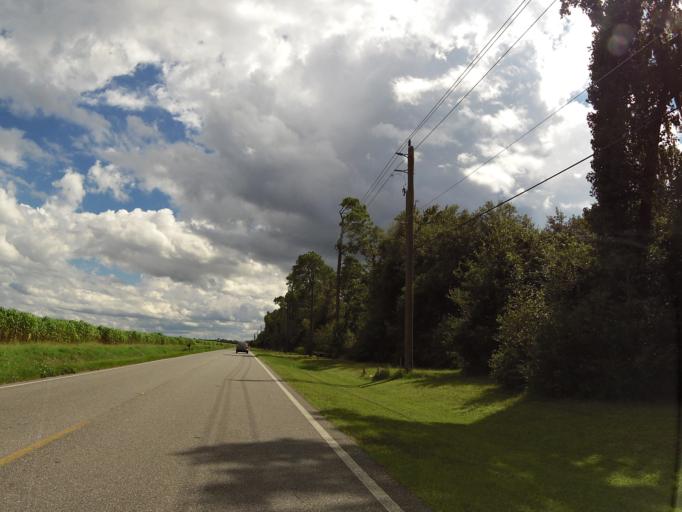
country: US
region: Florida
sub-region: Saint Johns County
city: Saint Augustine South
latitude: 29.8113
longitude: -81.4846
